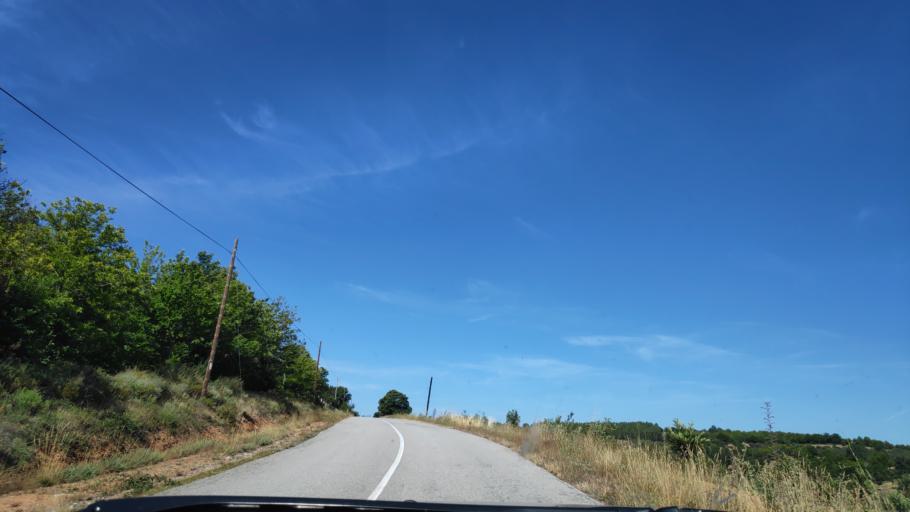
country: ES
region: Castille and Leon
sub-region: Provincia de Zamora
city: Alcanices
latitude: 41.6510
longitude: -6.3748
